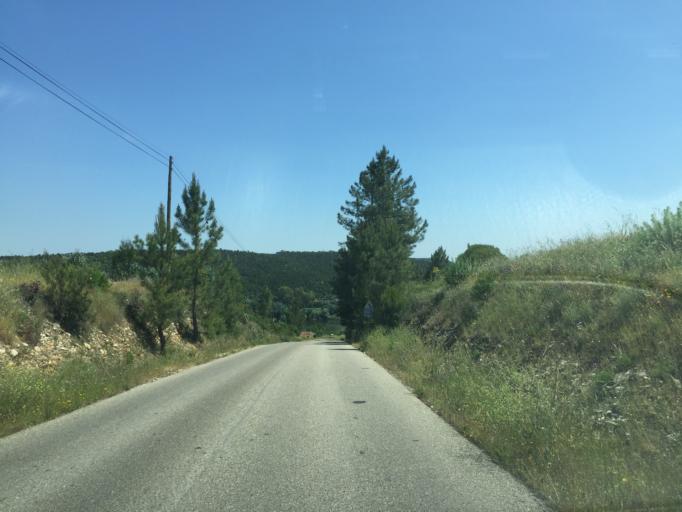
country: PT
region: Santarem
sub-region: Constancia
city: Constancia
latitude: 39.4698
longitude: -8.3473
